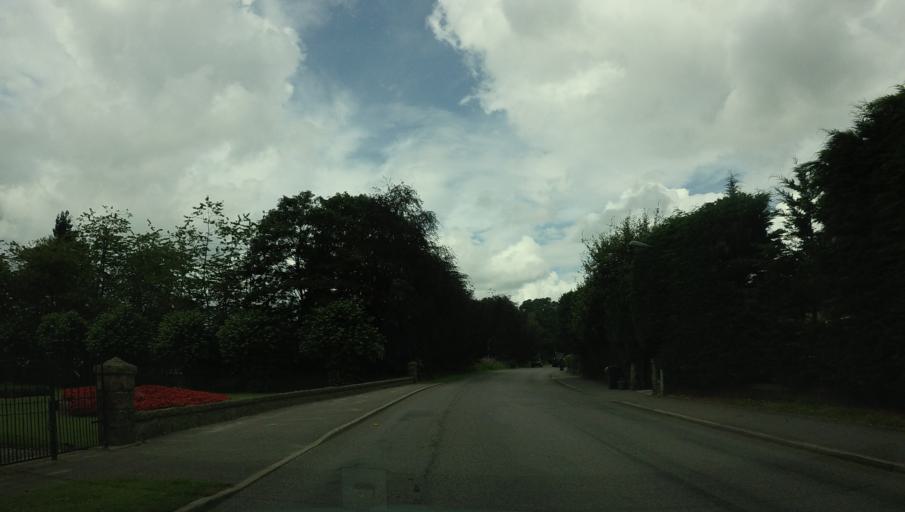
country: GB
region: Scotland
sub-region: Aberdeenshire
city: Banchory
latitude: 57.0520
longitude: -2.5107
